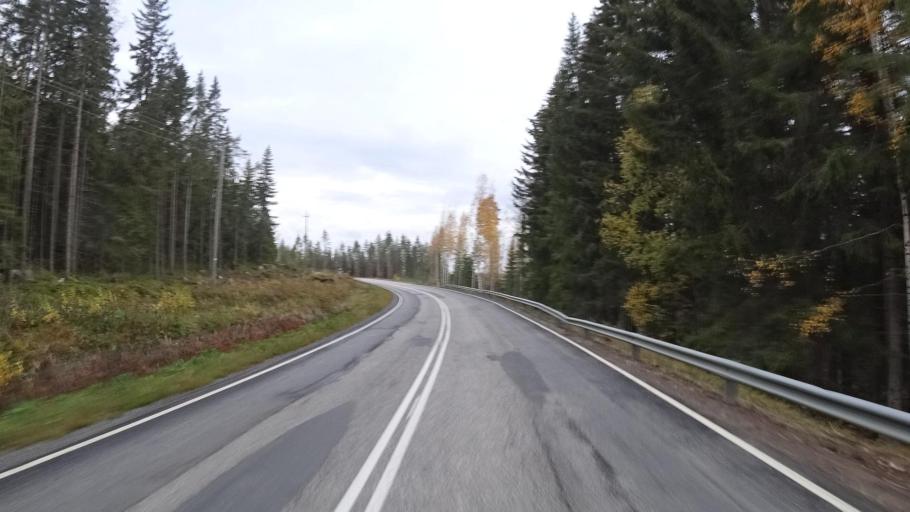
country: FI
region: Central Finland
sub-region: Joutsa
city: Joutsa
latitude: 61.8093
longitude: 26.1946
